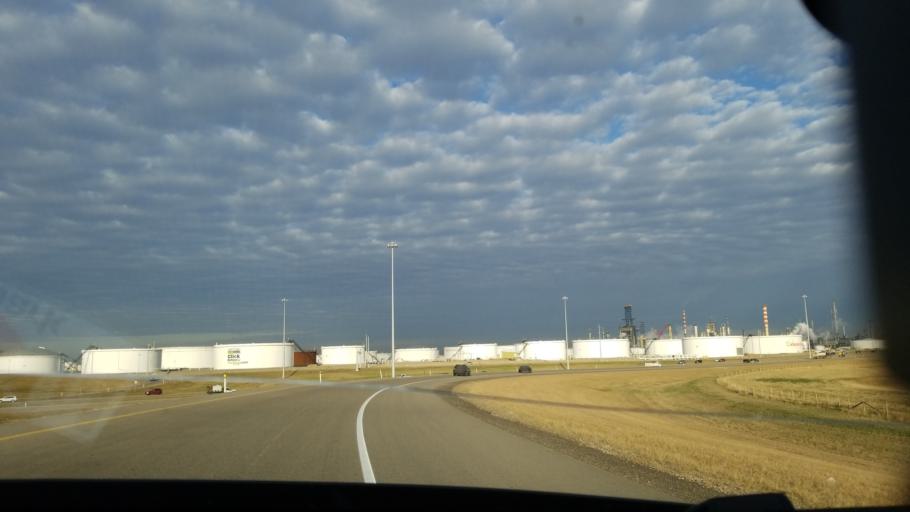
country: CA
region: Alberta
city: Sherwood Park
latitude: 53.5414
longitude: -113.3397
